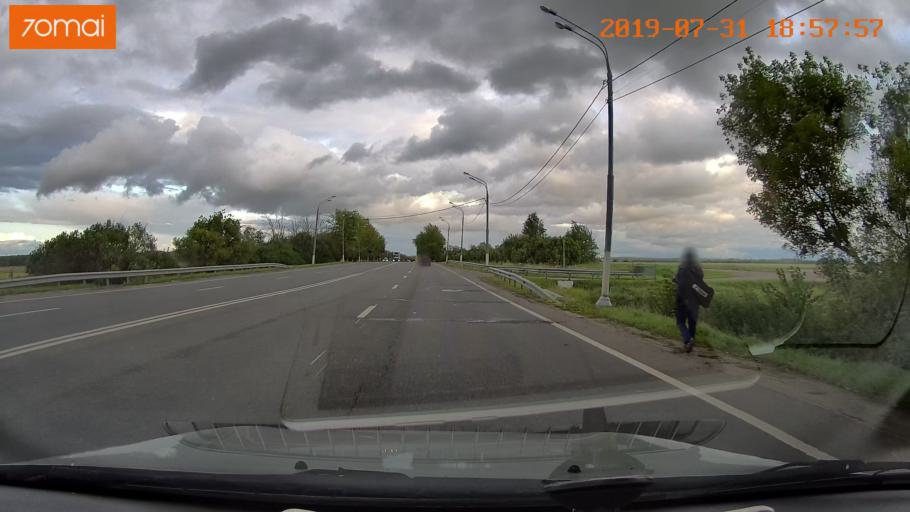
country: RU
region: Moskovskaya
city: Raduzhnyy
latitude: 55.1504
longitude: 38.6983
